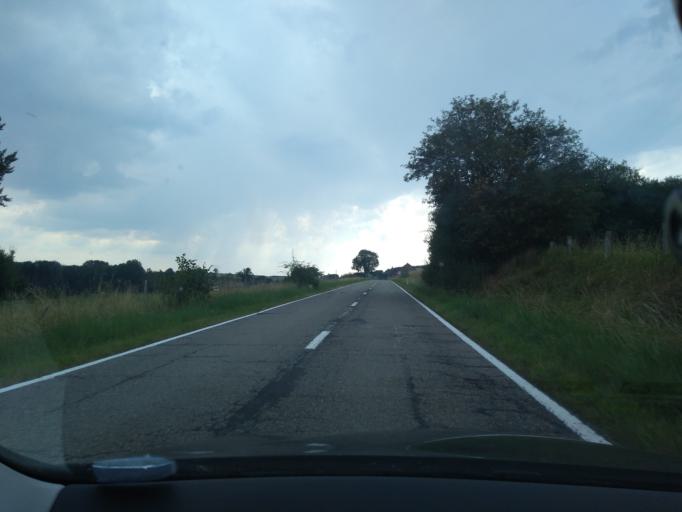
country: BE
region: Wallonia
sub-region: Province du Luxembourg
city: Bertogne
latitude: 50.0566
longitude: 5.6015
